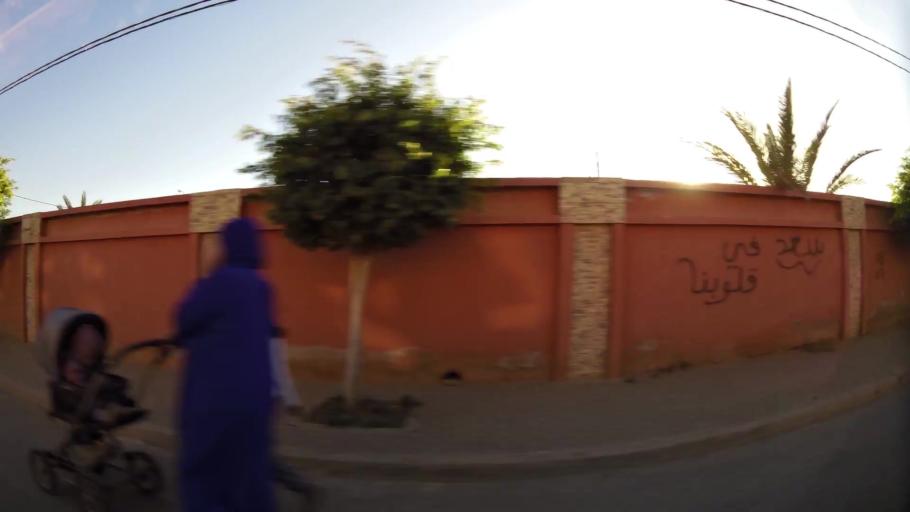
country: MA
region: Oriental
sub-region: Berkane-Taourirt
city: Berkane
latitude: 34.9273
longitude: -2.3193
